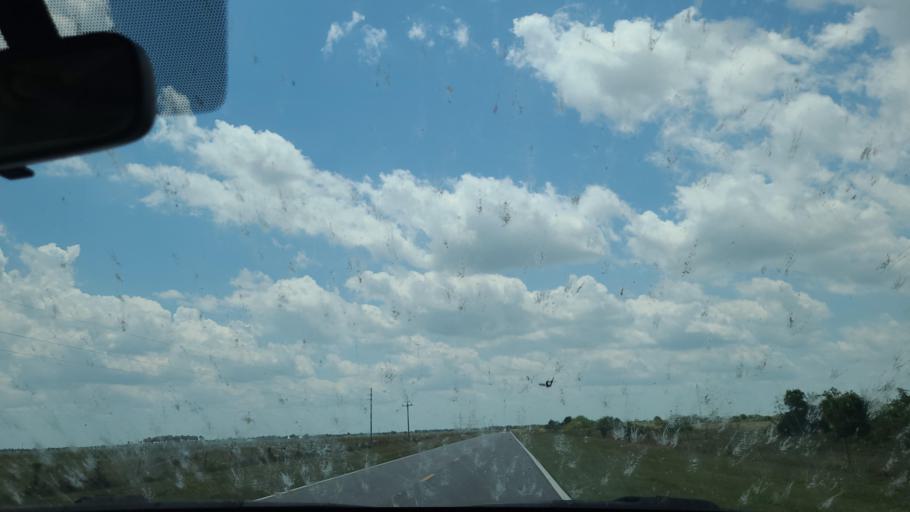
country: US
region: Florida
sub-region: Glades County
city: Buckhead Ridge
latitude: 27.2515
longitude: -81.0539
